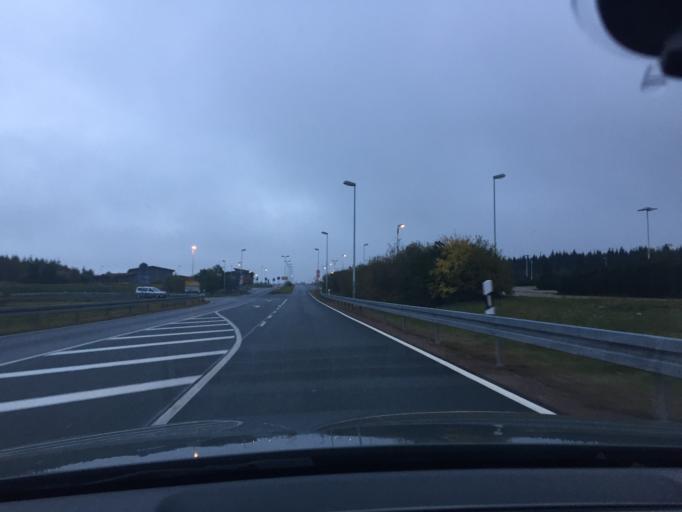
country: DE
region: Saxony
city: Altenberg
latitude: 50.7490
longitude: 13.7555
